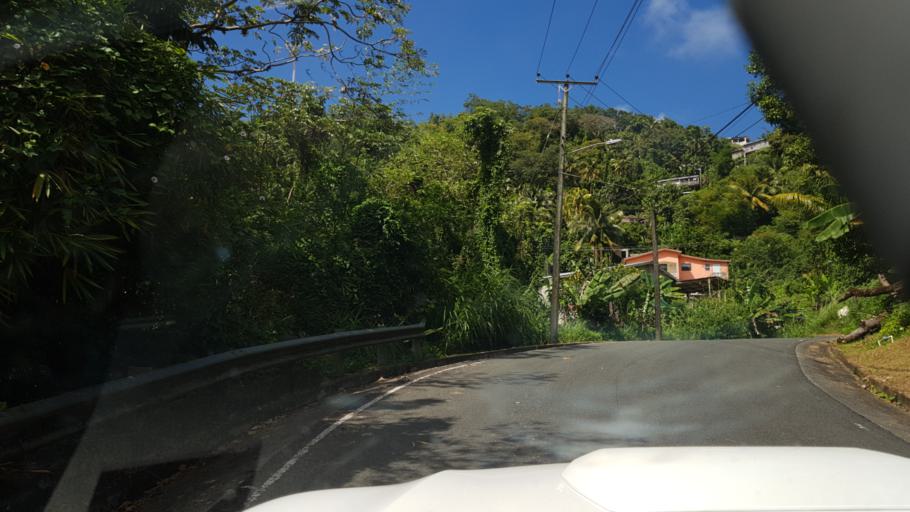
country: LC
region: Castries Quarter
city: Bisee
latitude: 13.9923
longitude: -60.9743
